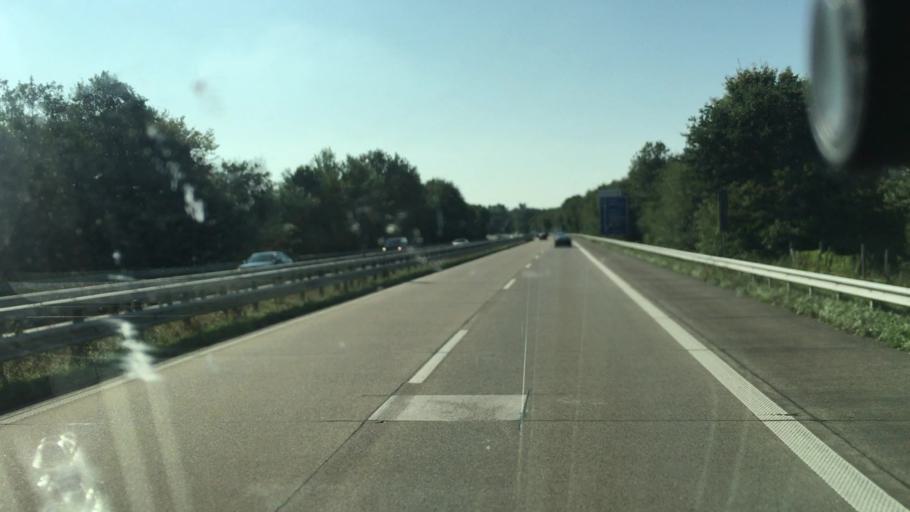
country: DE
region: Lower Saxony
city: Varel
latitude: 53.4041
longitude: 8.1000
